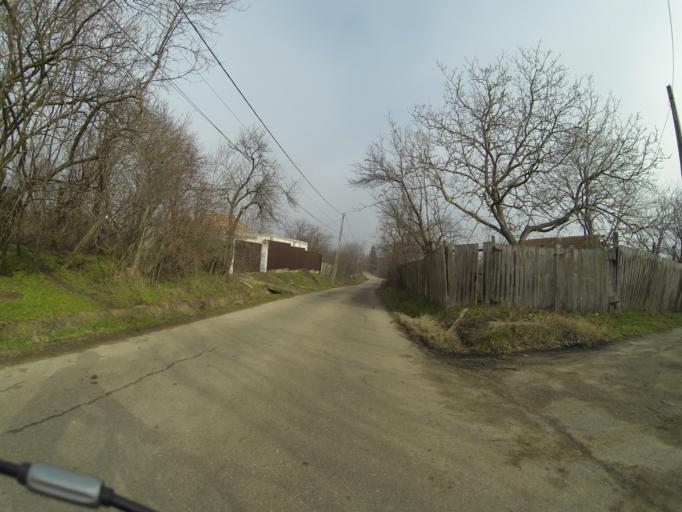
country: RO
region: Mehedinti
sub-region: Comuna Balacita
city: Gvardinita
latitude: 44.3906
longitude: 23.1419
